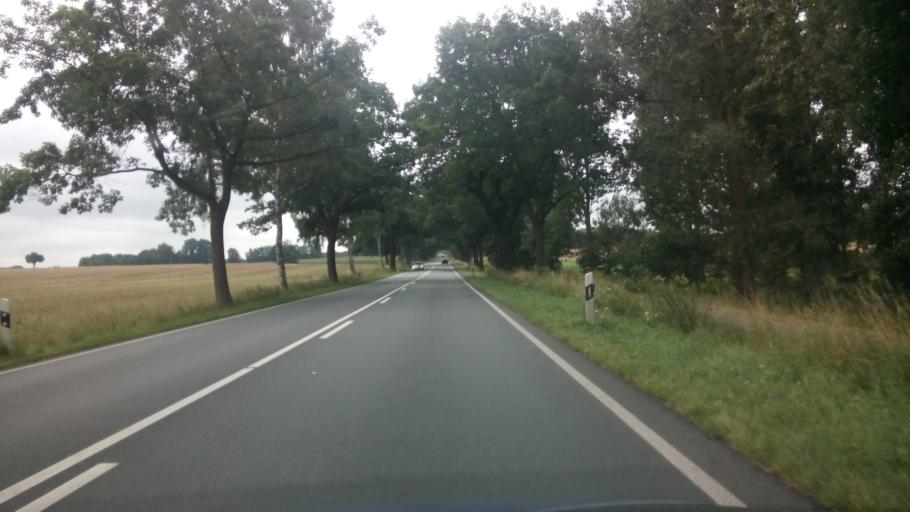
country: DE
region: Lower Saxony
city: Bassum
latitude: 52.8813
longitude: 8.7289
